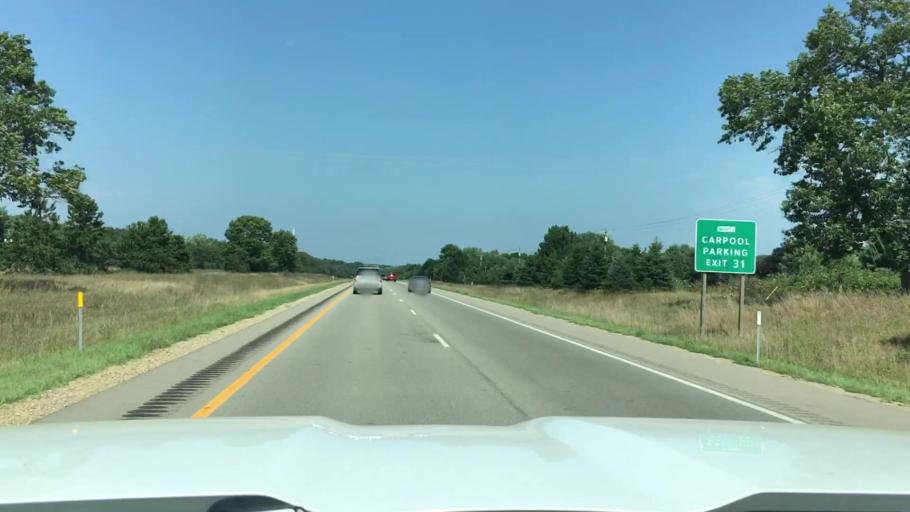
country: US
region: Michigan
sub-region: Kalamazoo County
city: Portage
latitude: 42.1861
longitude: -85.6458
